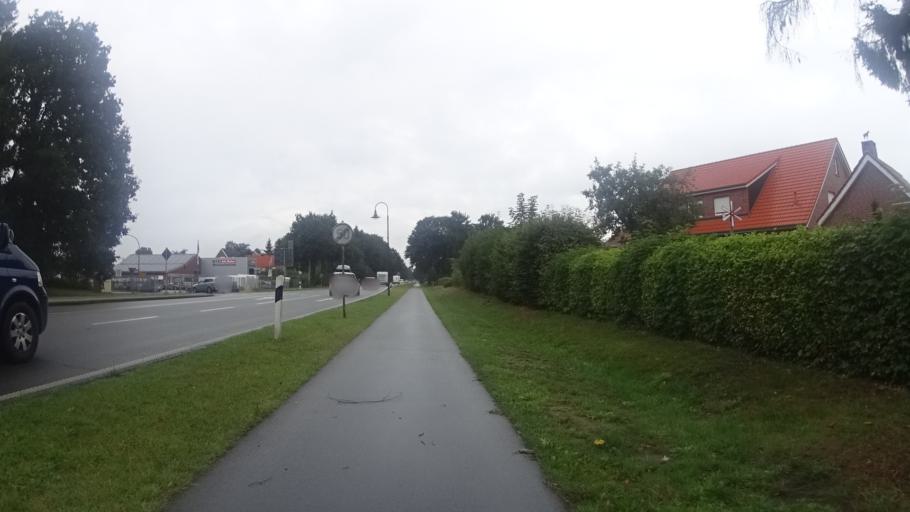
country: DE
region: Lower Saxony
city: Holtland
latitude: 53.2805
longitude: 7.5763
